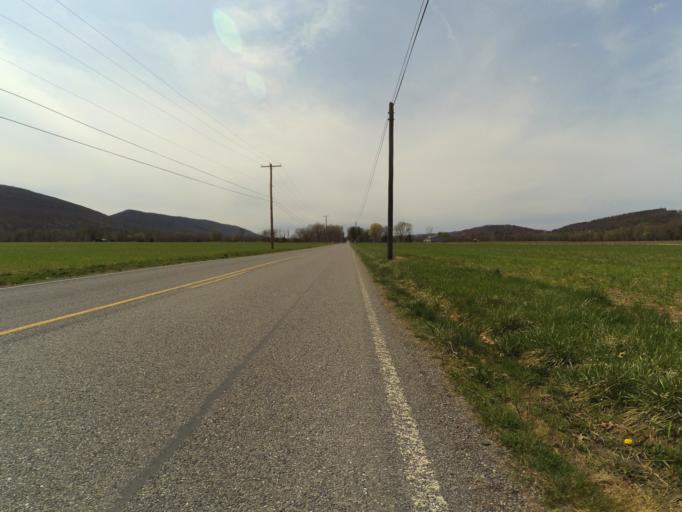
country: US
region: Pennsylvania
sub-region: Clinton County
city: Dunnstown
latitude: 41.1420
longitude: -77.4016
